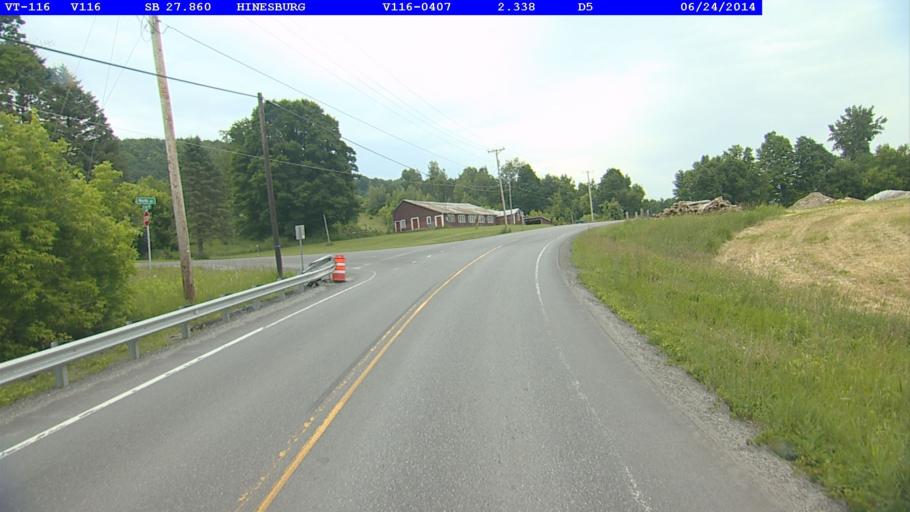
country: US
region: Vermont
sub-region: Chittenden County
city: Hinesburg
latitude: 44.3131
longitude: -73.0766
